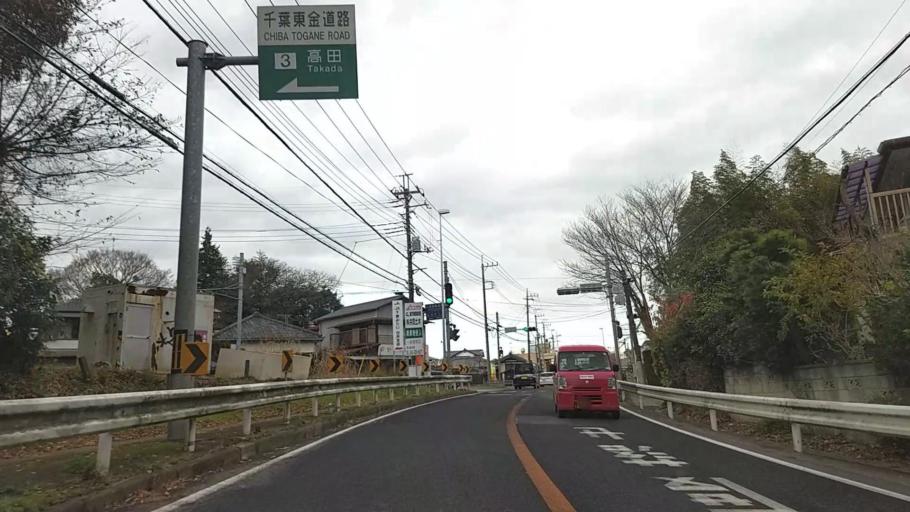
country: JP
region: Chiba
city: Yotsukaido
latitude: 35.5816
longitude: 140.2327
